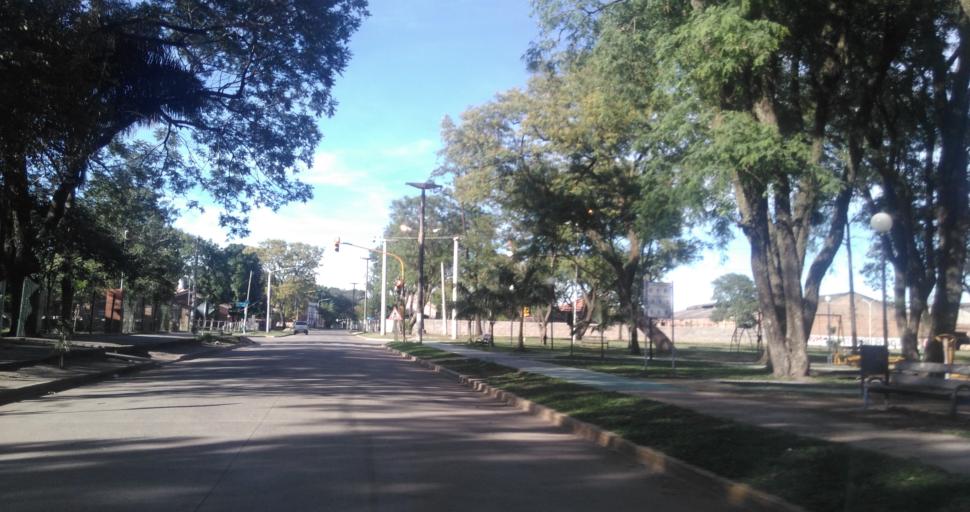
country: AR
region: Chaco
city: Fontana
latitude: -27.4159
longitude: -59.0302
